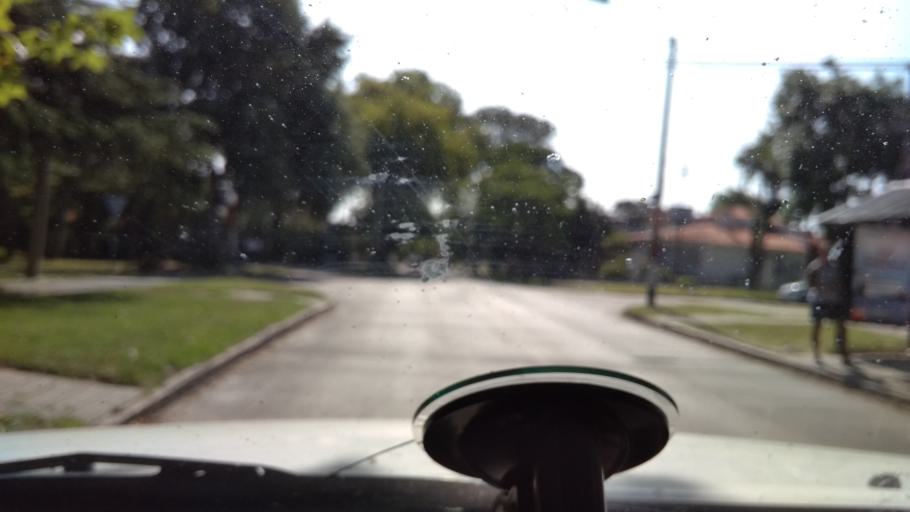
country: UY
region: Canelones
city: Paso de Carrasco
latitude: -34.8908
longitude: -56.0767
